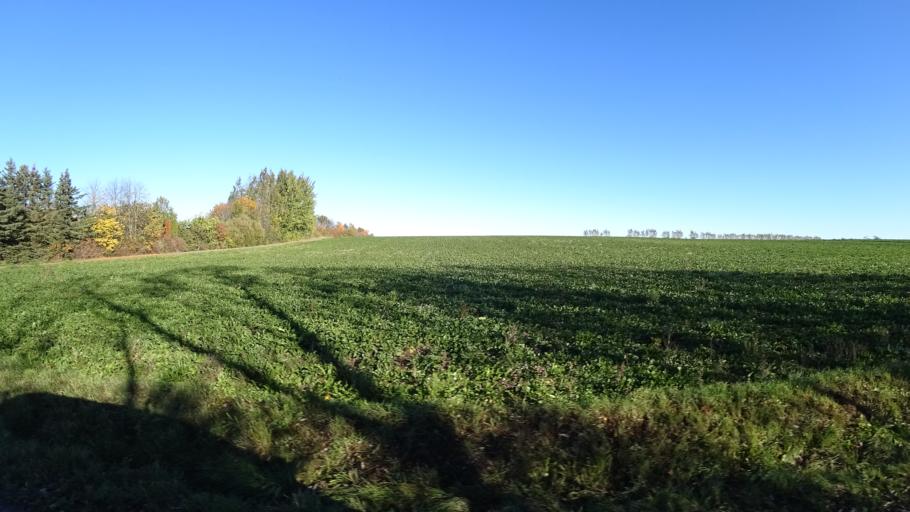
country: SE
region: Skane
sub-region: Svedala Kommun
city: Klagerup
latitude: 55.6274
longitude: 13.3128
